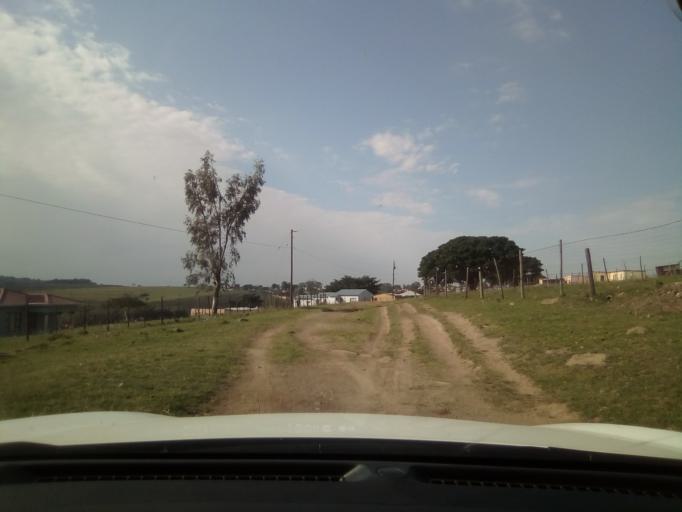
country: ZA
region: Eastern Cape
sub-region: Buffalo City Metropolitan Municipality
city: Bhisho
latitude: -32.9827
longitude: 27.2598
